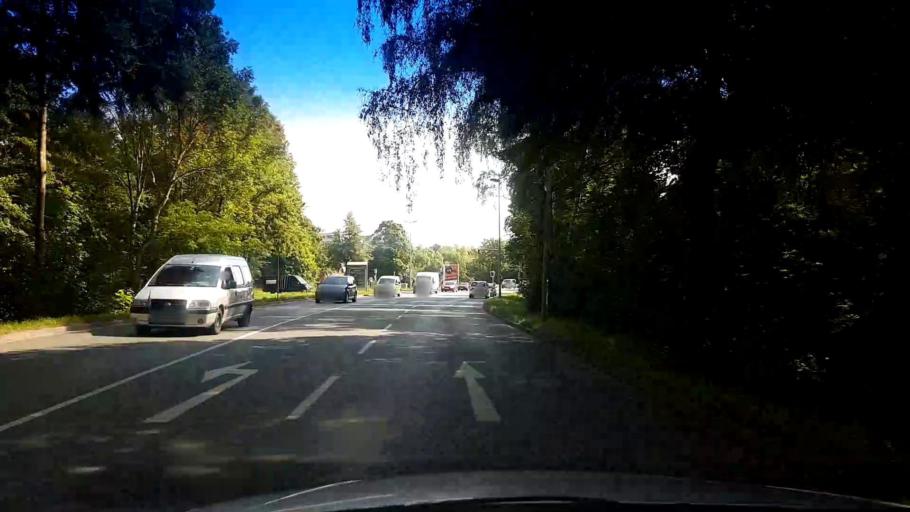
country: DE
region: Bavaria
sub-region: Upper Franconia
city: Heinersreuth
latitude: 49.9349
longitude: 11.5422
